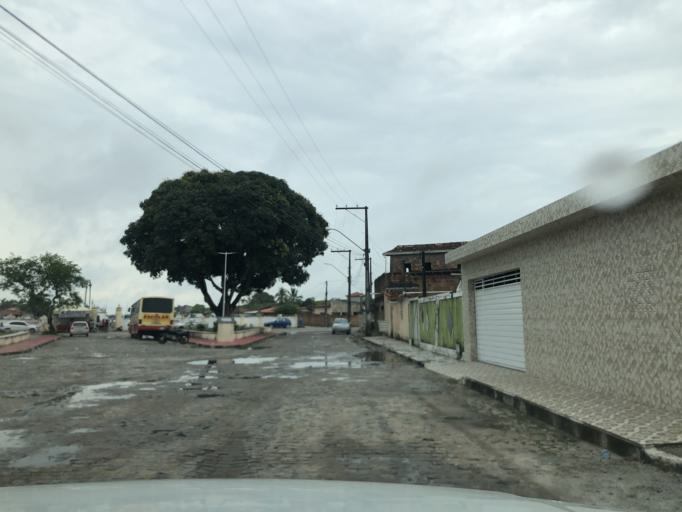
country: BR
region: Bahia
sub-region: Esplanada
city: Esplanada
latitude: -11.7934
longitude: -37.9518
